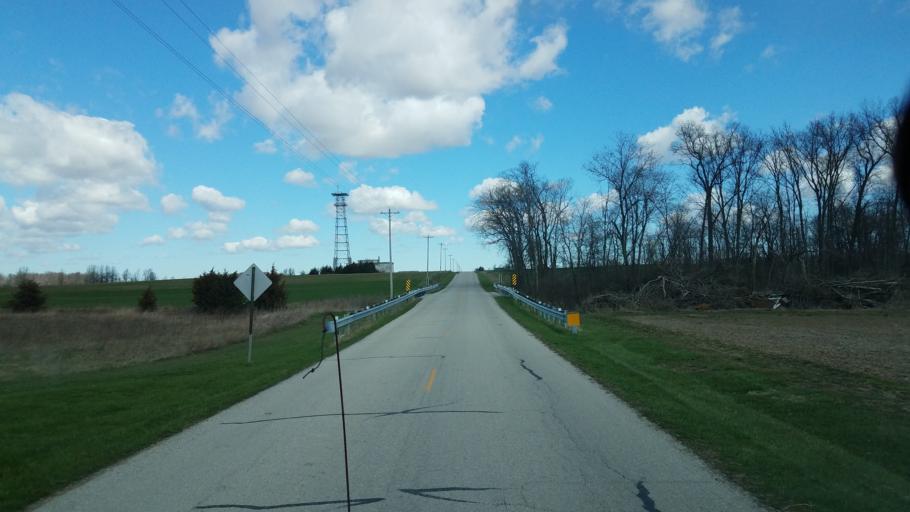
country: US
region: Ohio
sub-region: Sandusky County
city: Mount Carmel
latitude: 41.1264
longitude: -82.9384
